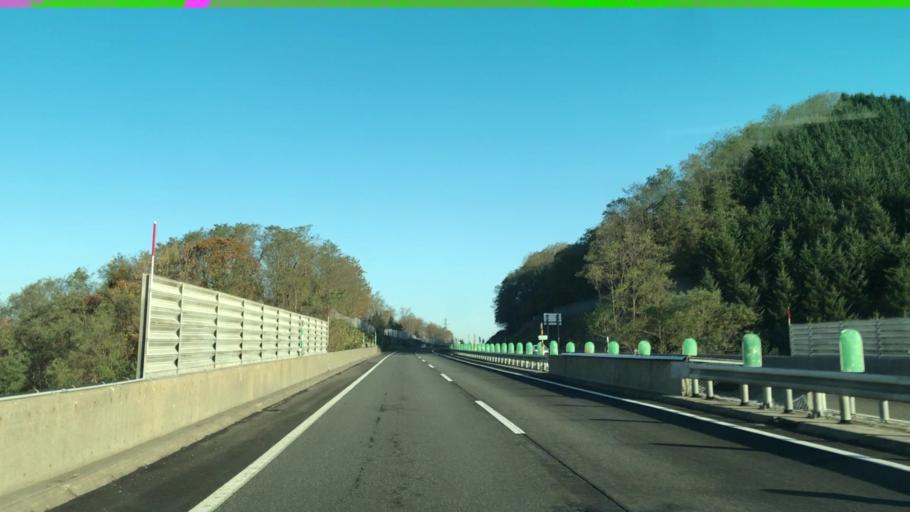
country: JP
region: Hokkaido
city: Sunagawa
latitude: 43.4179
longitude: 141.9110
